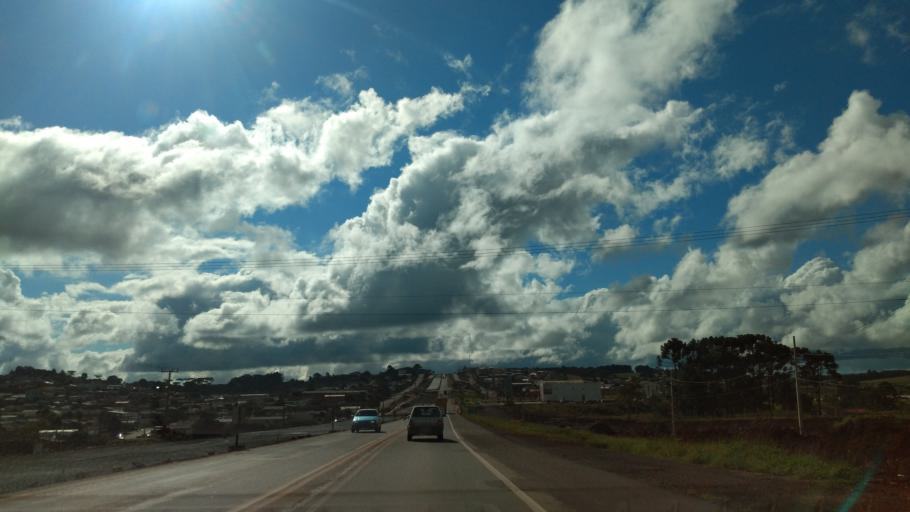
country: BR
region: Parana
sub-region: Guarapuava
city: Guarapuava
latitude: -25.3555
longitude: -51.4838
